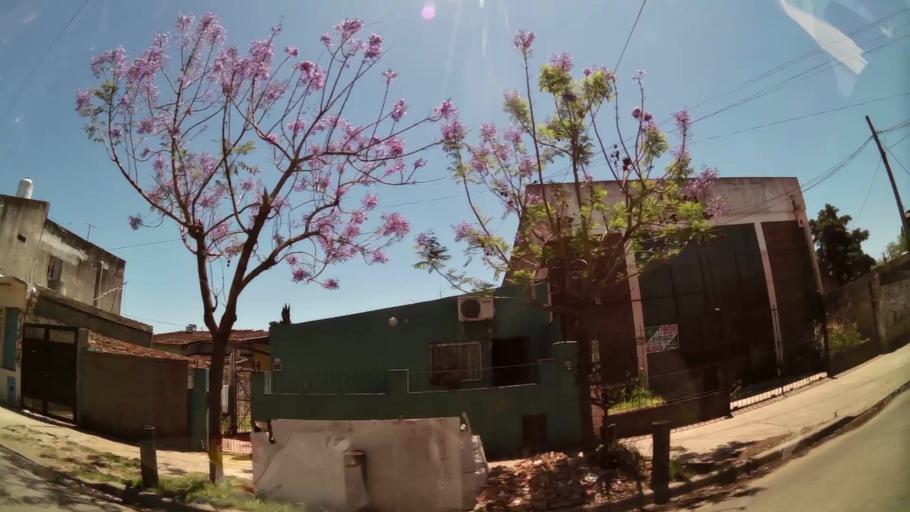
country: AR
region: Buenos Aires
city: Hurlingham
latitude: -34.5104
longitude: -58.7046
